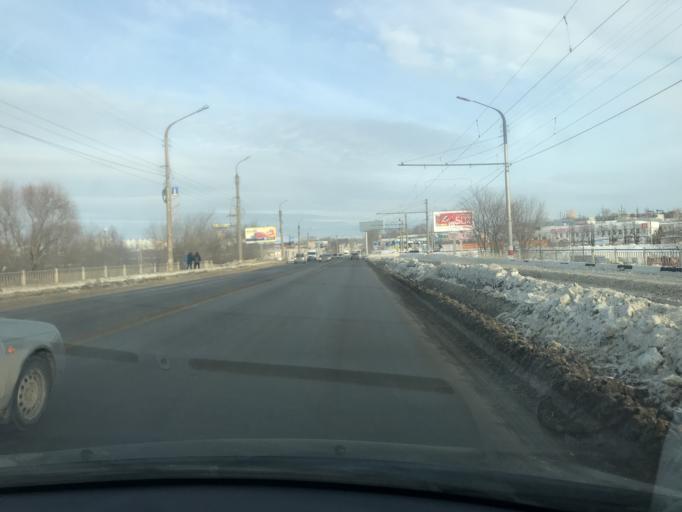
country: RU
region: Ulyanovsk
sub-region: Ulyanovskiy Rayon
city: Ulyanovsk
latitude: 54.3252
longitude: 48.3572
